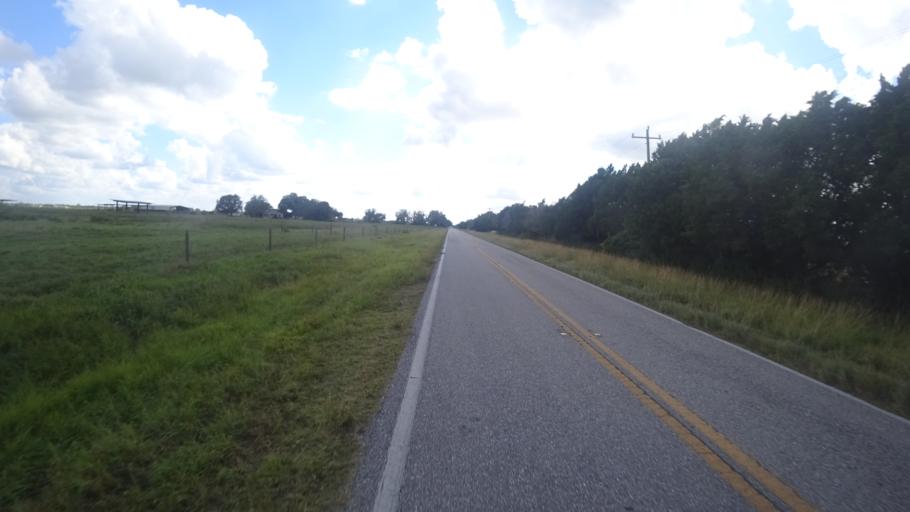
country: US
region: Florida
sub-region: DeSoto County
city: Arcadia
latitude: 27.2936
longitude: -82.1134
